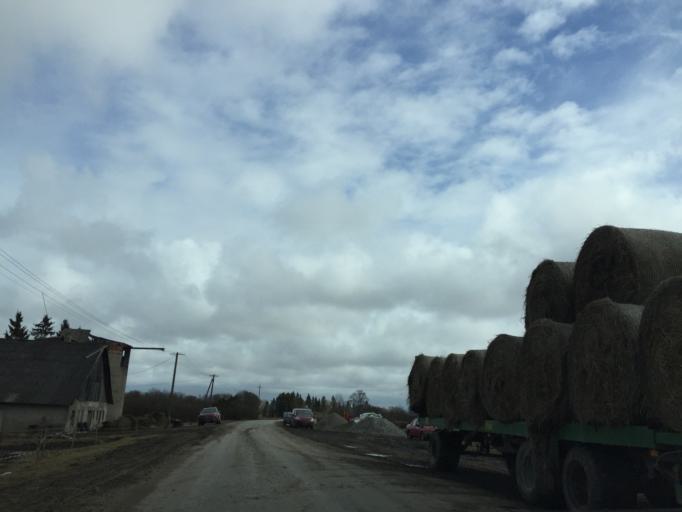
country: EE
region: Laeaene
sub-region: Lihula vald
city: Lihula
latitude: 58.7331
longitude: 23.8649
